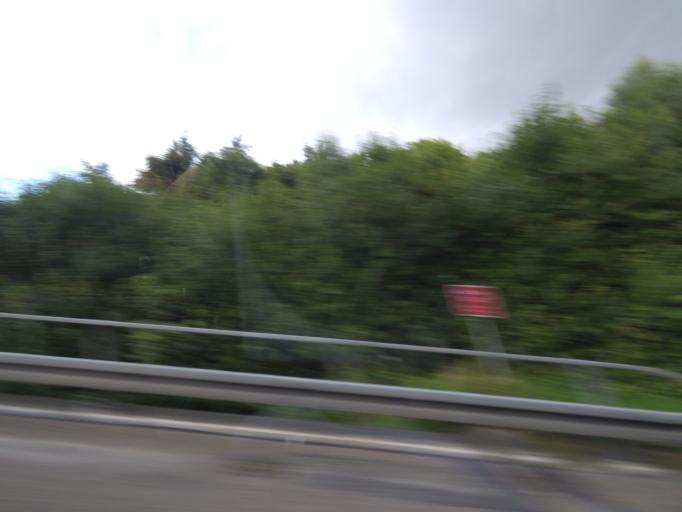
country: DK
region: South Denmark
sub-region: Fredericia Kommune
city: Taulov
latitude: 55.5633
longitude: 9.6203
